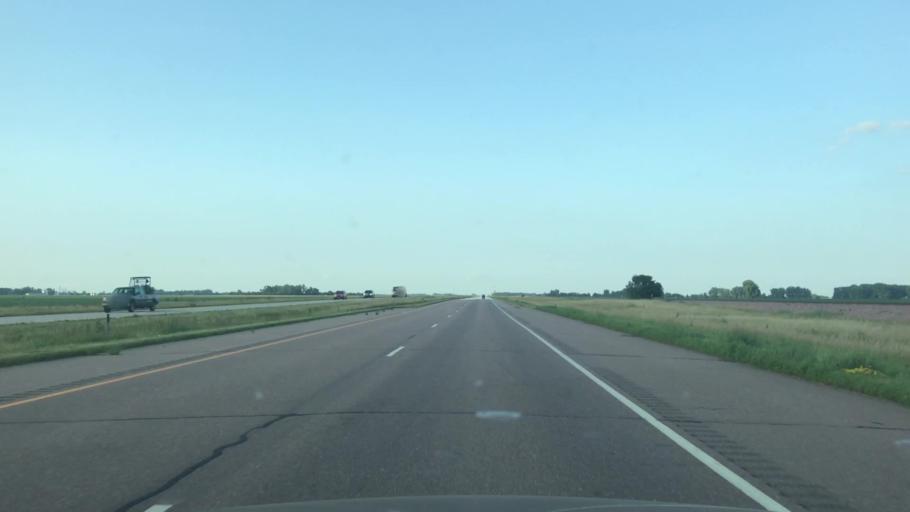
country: US
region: Minnesota
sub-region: Nobles County
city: Worthington
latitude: 43.7349
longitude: -95.4155
